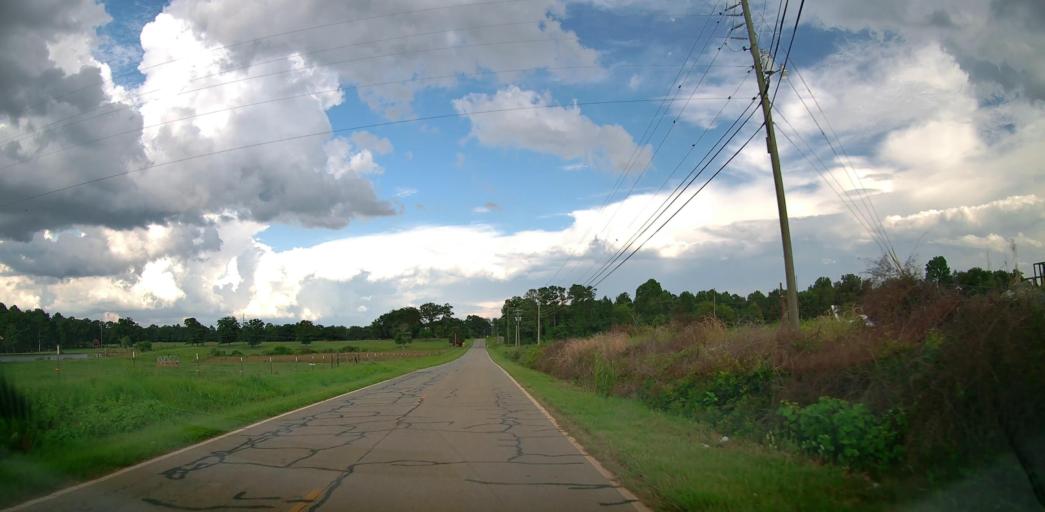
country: US
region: Georgia
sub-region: Bleckley County
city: Cochran
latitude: 32.3958
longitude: -83.3687
